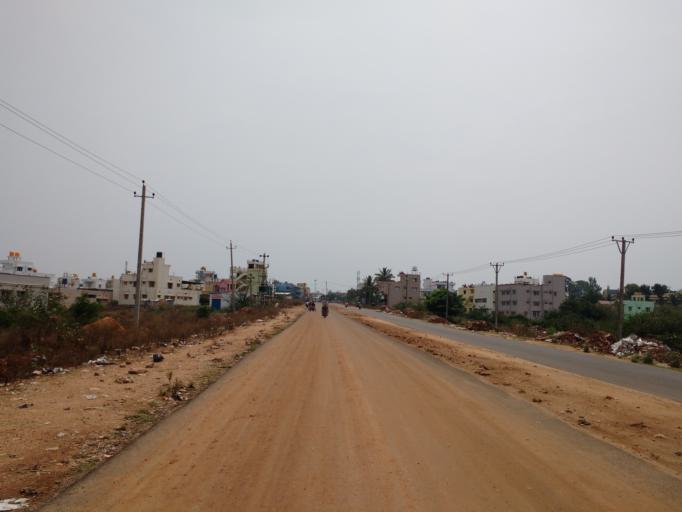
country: IN
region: Karnataka
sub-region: Hassan
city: Hassan
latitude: 13.0256
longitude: 76.0974
